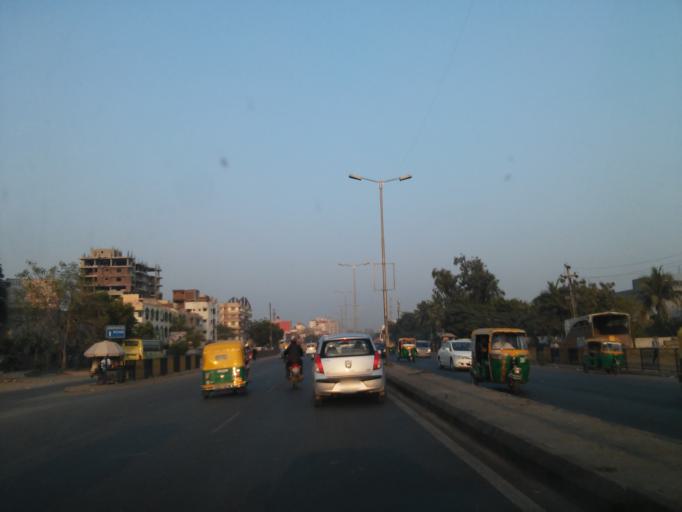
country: IN
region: Gujarat
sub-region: Ahmadabad
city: Sarkhej
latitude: 22.9906
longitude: 72.5167
